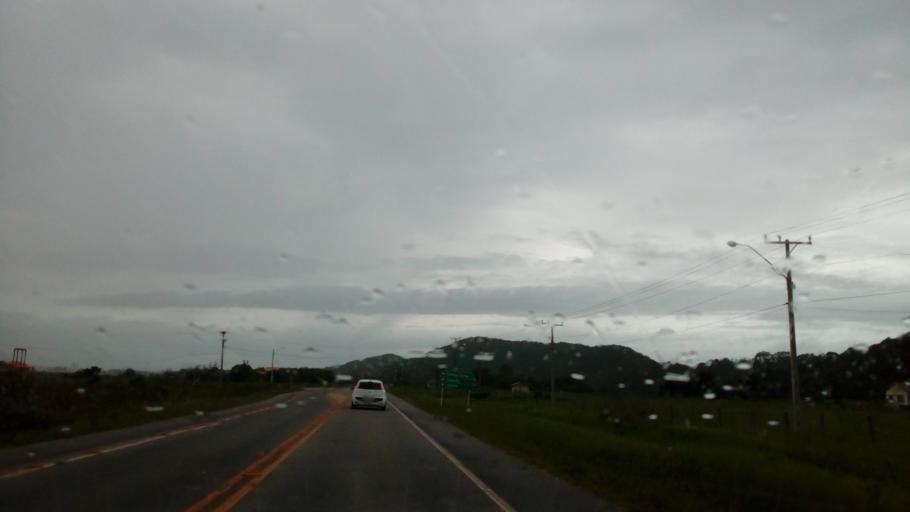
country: BR
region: Santa Catarina
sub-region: Laguna
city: Laguna
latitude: -28.5282
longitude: -48.7786
